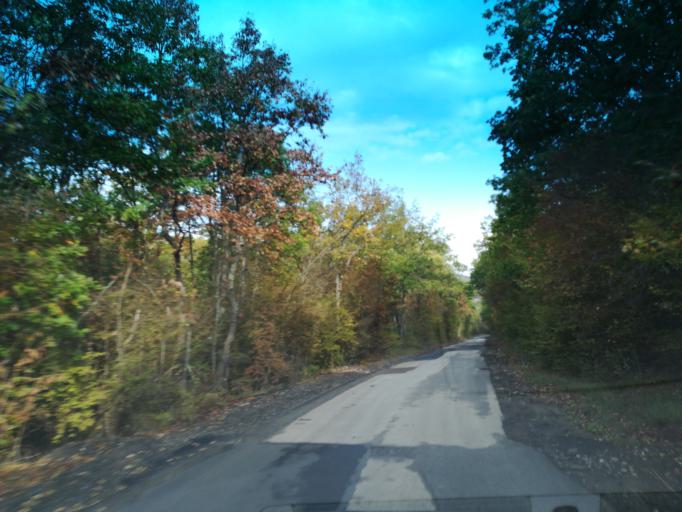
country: BG
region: Stara Zagora
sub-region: Obshtina Nikolaevo
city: Elkhovo
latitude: 42.3238
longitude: 25.3984
